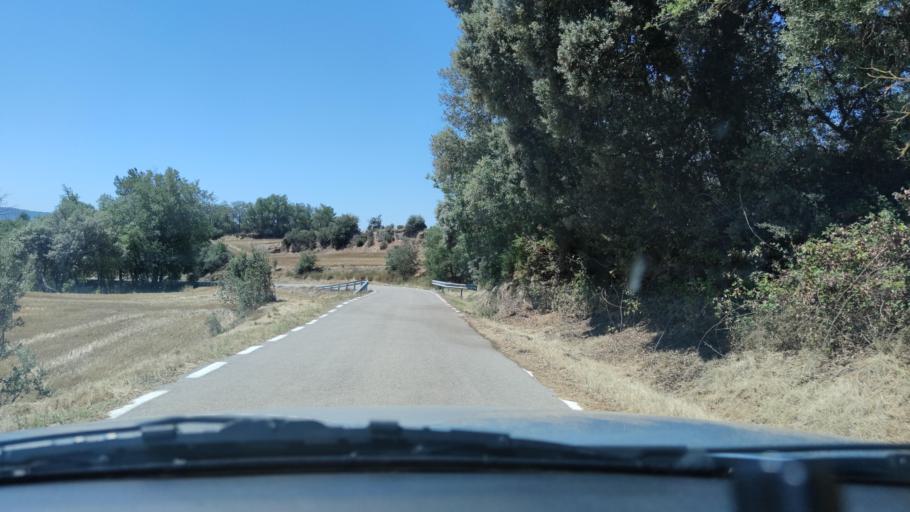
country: ES
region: Catalonia
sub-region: Provincia de Lleida
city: Tora de Riubregos
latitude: 41.8531
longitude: 1.4286
